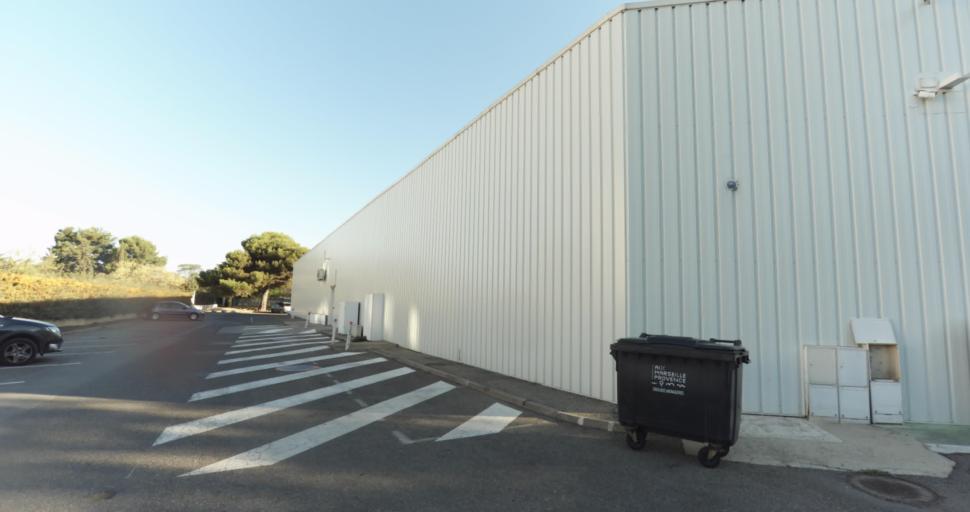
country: FR
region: Provence-Alpes-Cote d'Azur
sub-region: Departement des Bouches-du-Rhone
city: Miramas
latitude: 43.5888
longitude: 5.0026
